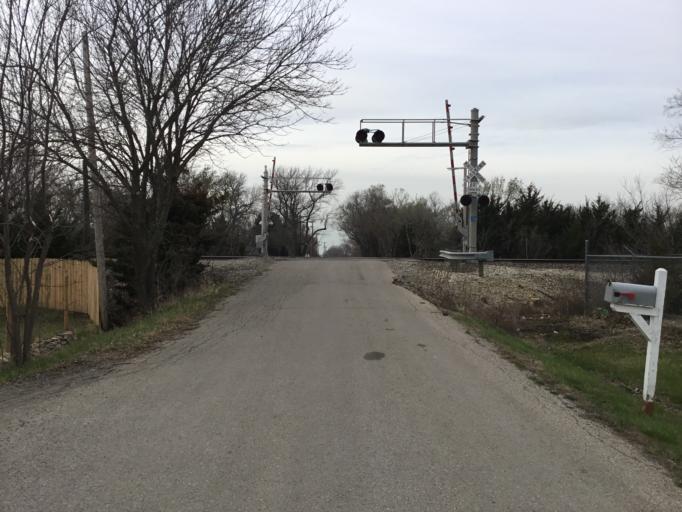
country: US
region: Kansas
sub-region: Lyon County
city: Emporia
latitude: 38.4012
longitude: -96.1618
